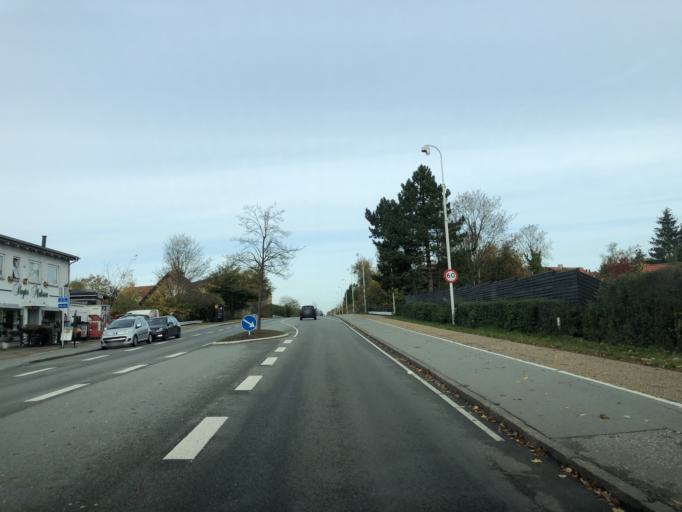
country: DK
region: Capital Region
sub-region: Rudersdal Kommune
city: Birkerod
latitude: 55.8466
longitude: 12.4297
